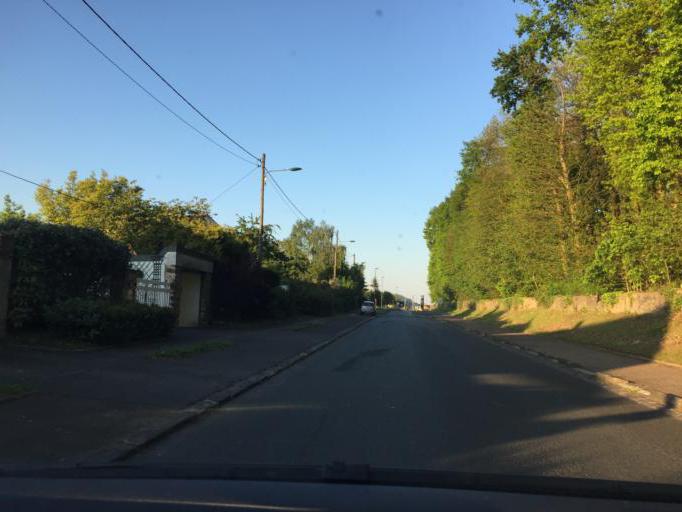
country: FR
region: Ile-de-France
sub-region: Departement de l'Essonne
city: Orsay
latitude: 48.6982
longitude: 2.2045
